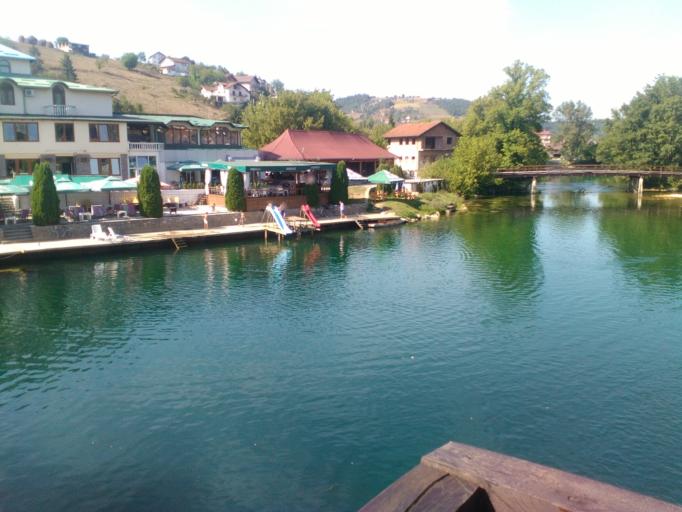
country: BA
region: Federation of Bosnia and Herzegovina
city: Bosanska Krupa
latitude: 44.8859
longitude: 16.1548
